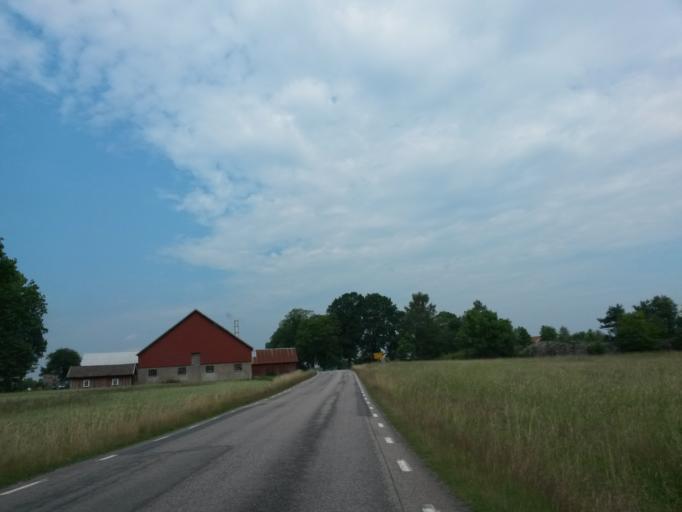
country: SE
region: Vaestra Goetaland
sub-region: Essunga Kommun
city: Nossebro
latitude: 58.1362
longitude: 12.7750
